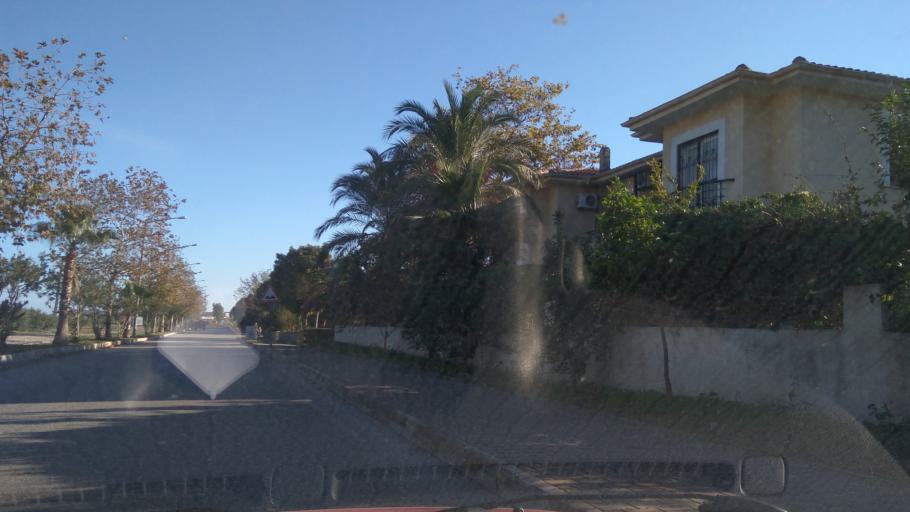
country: TR
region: Antalya
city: Kemer
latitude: 36.5696
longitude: 30.5594
